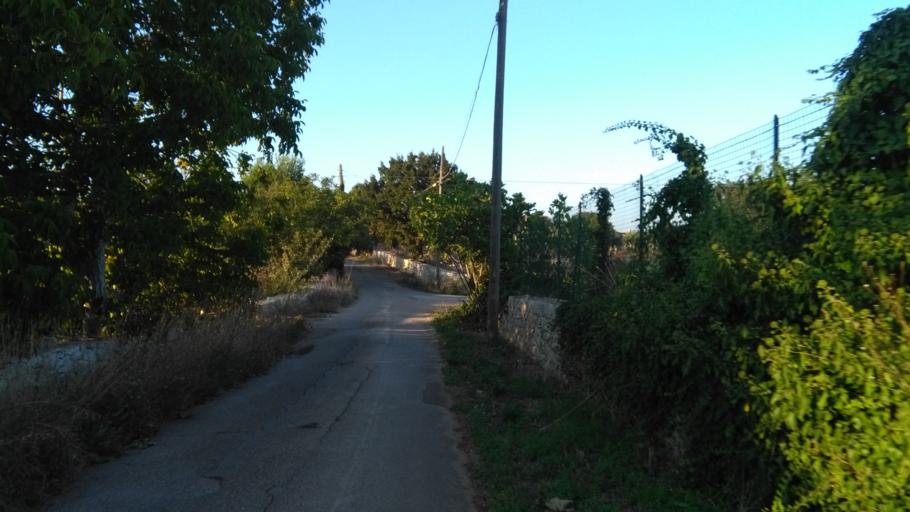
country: IT
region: Apulia
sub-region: Provincia di Bari
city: Putignano
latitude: 40.8259
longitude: 17.0924
